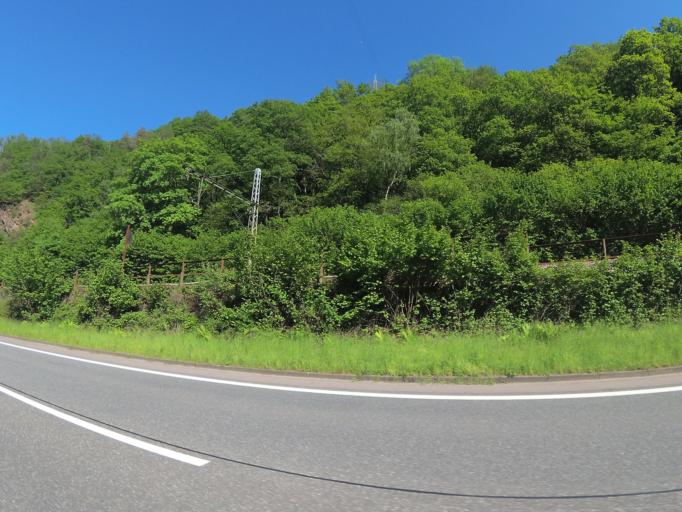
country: DE
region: Saarland
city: Mettlach
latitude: 49.5075
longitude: 6.5942
